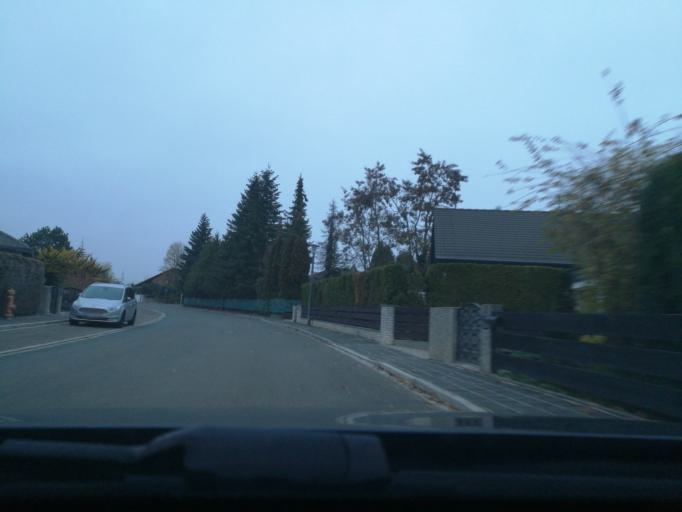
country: DE
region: Bavaria
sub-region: Regierungsbezirk Mittelfranken
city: Obermichelbach
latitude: 49.5320
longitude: 10.9135
